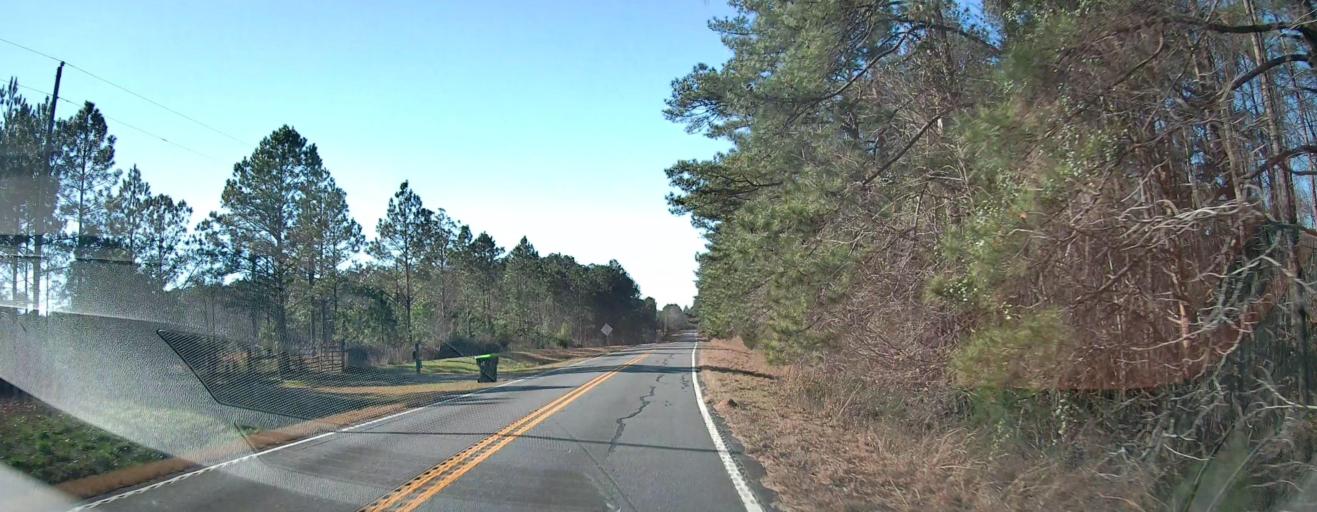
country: US
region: Georgia
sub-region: Talbot County
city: Talbotton
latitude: 32.6460
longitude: -84.4377
